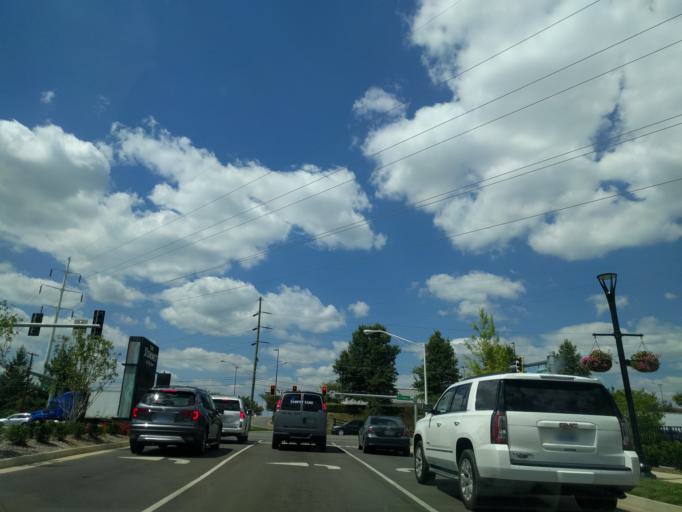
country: US
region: Kentucky
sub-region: Fayette County
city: Monticello
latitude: 37.9783
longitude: -84.5286
